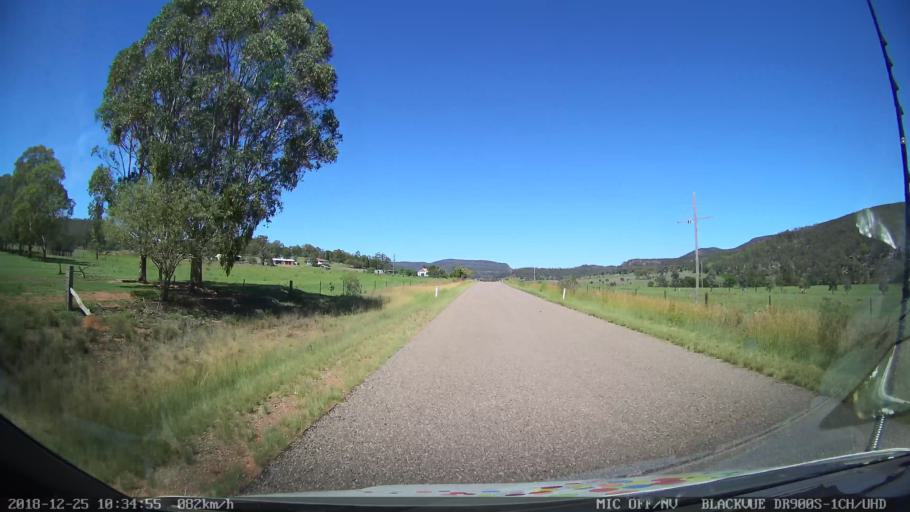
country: AU
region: New South Wales
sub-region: Upper Hunter Shire
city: Merriwa
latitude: -32.3947
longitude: 150.4018
